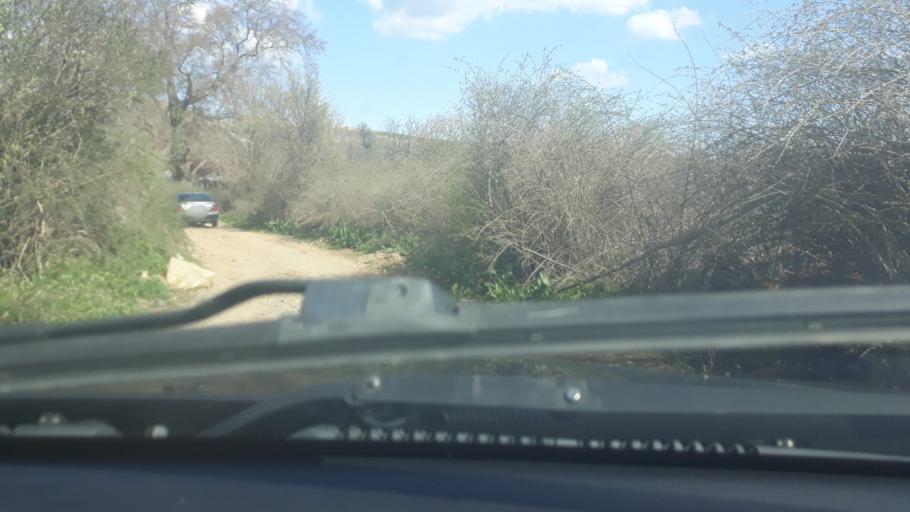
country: MK
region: Caska
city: Caska
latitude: 41.6754
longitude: 21.6809
